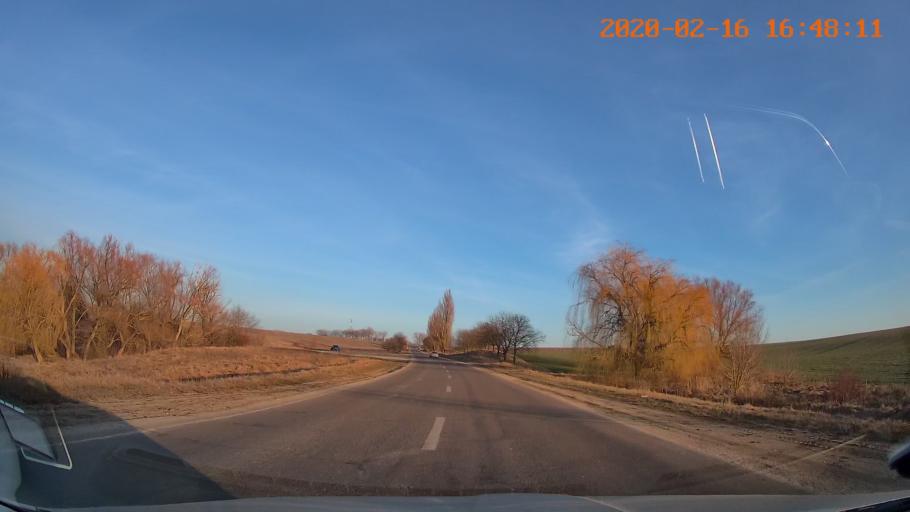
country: RO
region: Botosani
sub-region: Comuna Radauti-Prut
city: Miorcani
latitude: 48.2867
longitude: 26.8901
